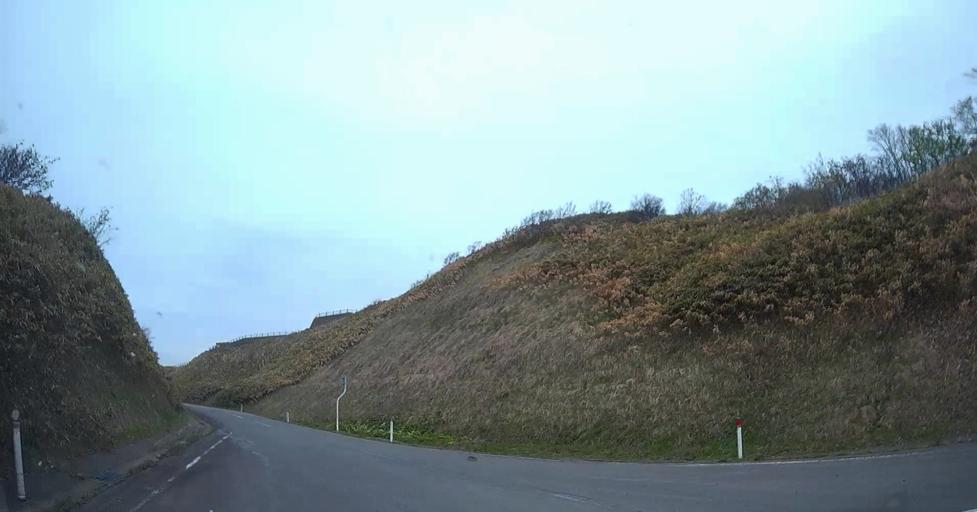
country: JP
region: Aomori
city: Shimokizukuri
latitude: 41.2129
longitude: 140.3564
